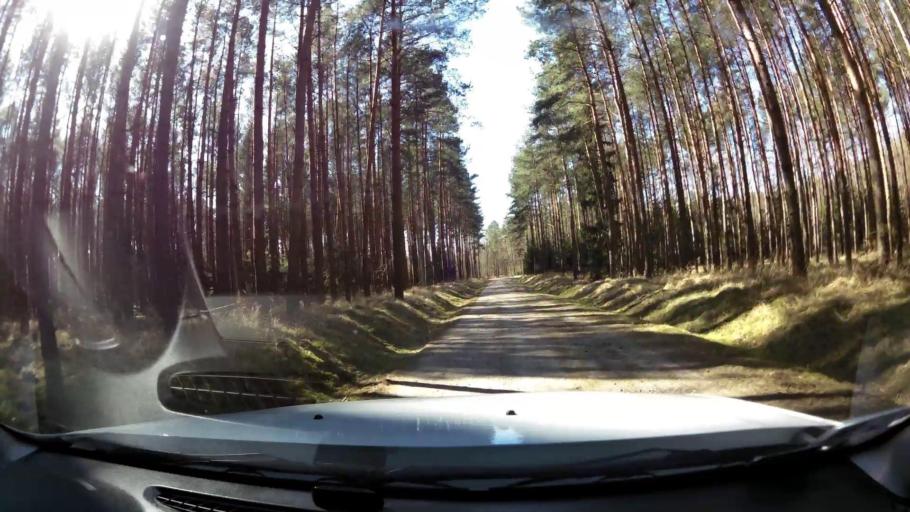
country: PL
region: West Pomeranian Voivodeship
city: Trzcinsko Zdroj
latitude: 53.0098
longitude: 14.6167
